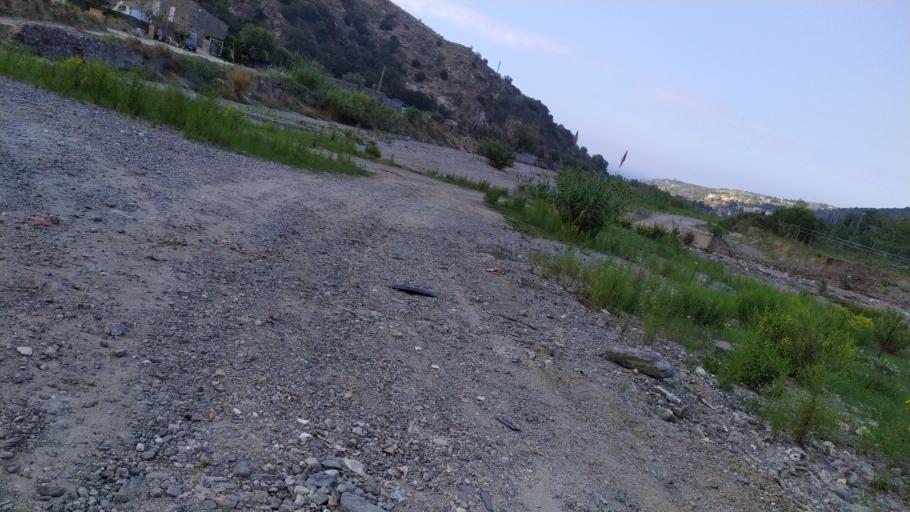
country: IT
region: Sicily
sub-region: Messina
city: Saponara
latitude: 38.1954
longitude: 15.4297
